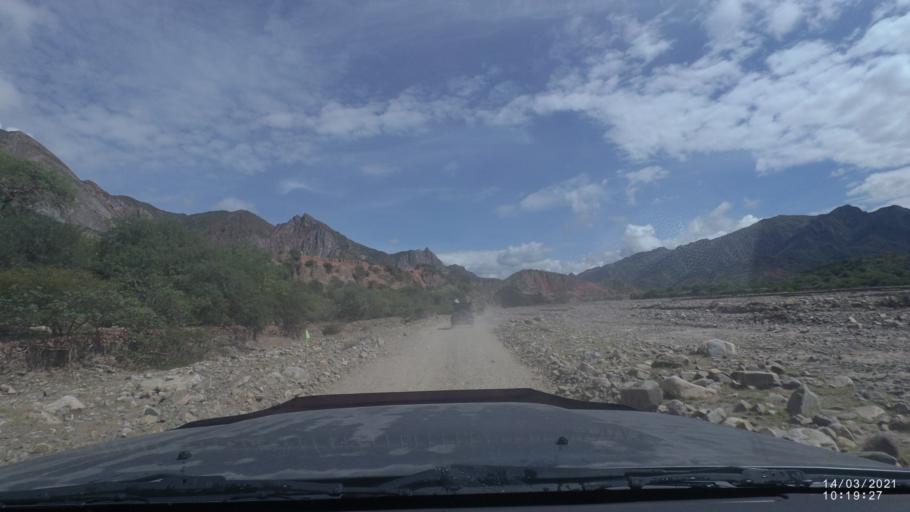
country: BO
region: Cochabamba
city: Cliza
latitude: -17.9322
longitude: -65.8692
